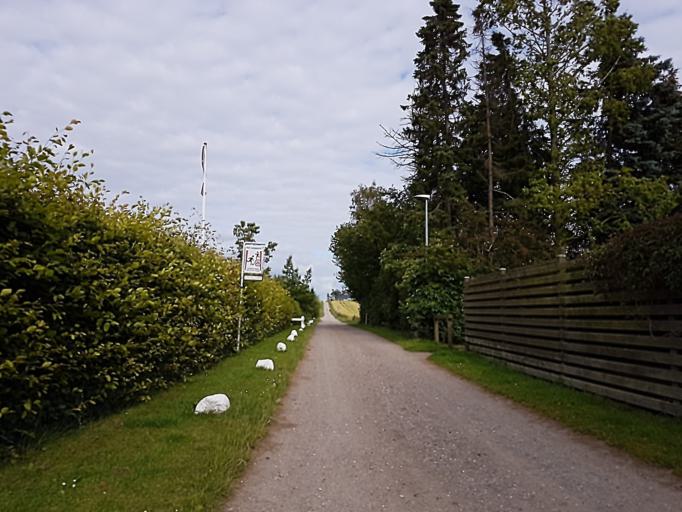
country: DK
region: Capital Region
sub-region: Egedal Kommune
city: Ganlose
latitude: 55.7935
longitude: 12.2734
